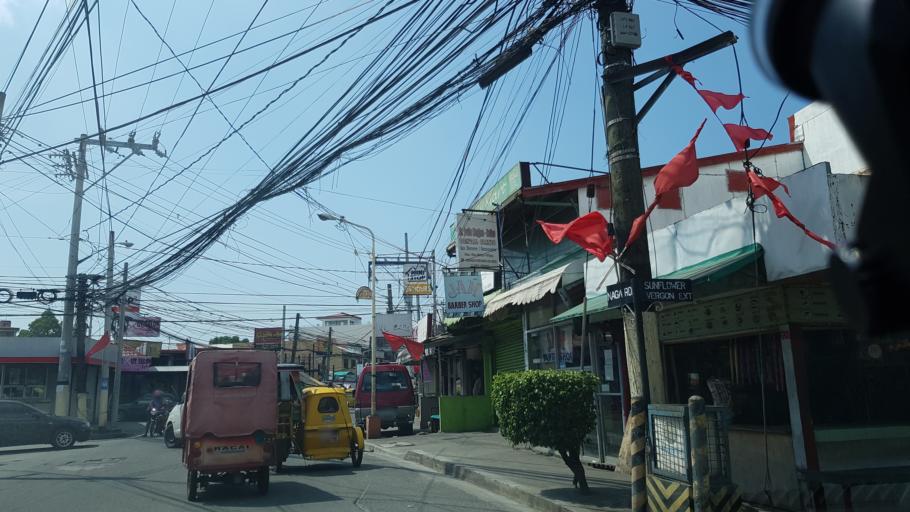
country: PH
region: Calabarzon
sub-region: Province of Rizal
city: Las Pinas
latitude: 14.4678
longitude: 120.9814
